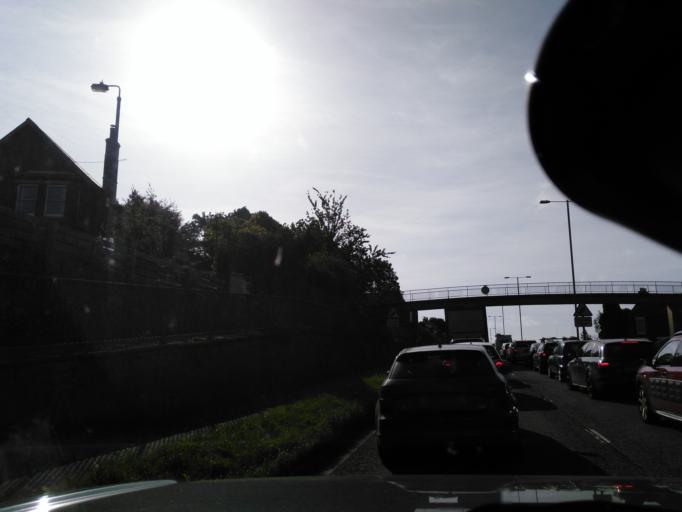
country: GB
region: England
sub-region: Wiltshire
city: Salisbury
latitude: 51.0762
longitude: -1.7913
